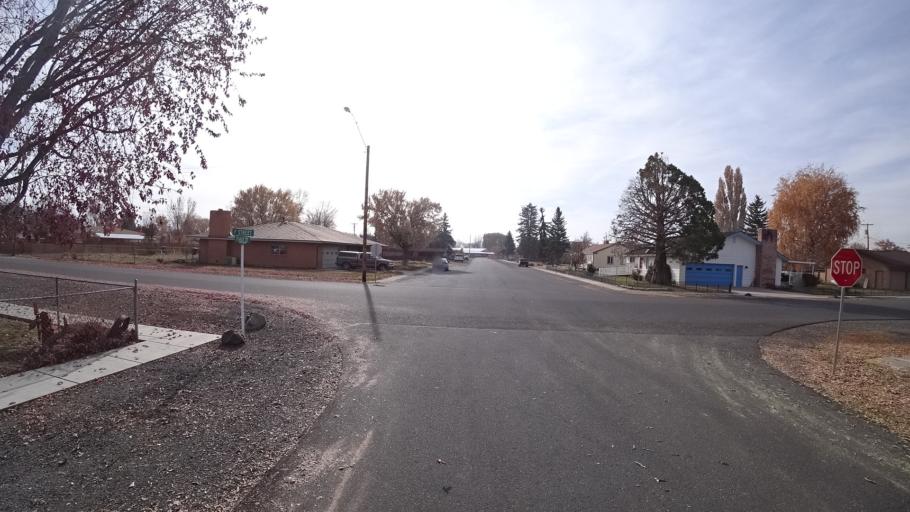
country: US
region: California
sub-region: Siskiyou County
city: Tulelake
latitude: 41.9525
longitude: -121.4792
